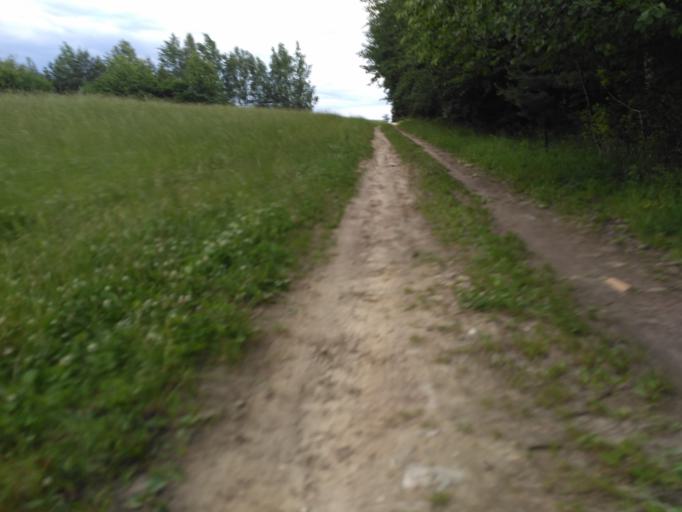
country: DE
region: Brandenburg
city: Hohenleipisch
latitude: 51.4978
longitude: 13.5247
